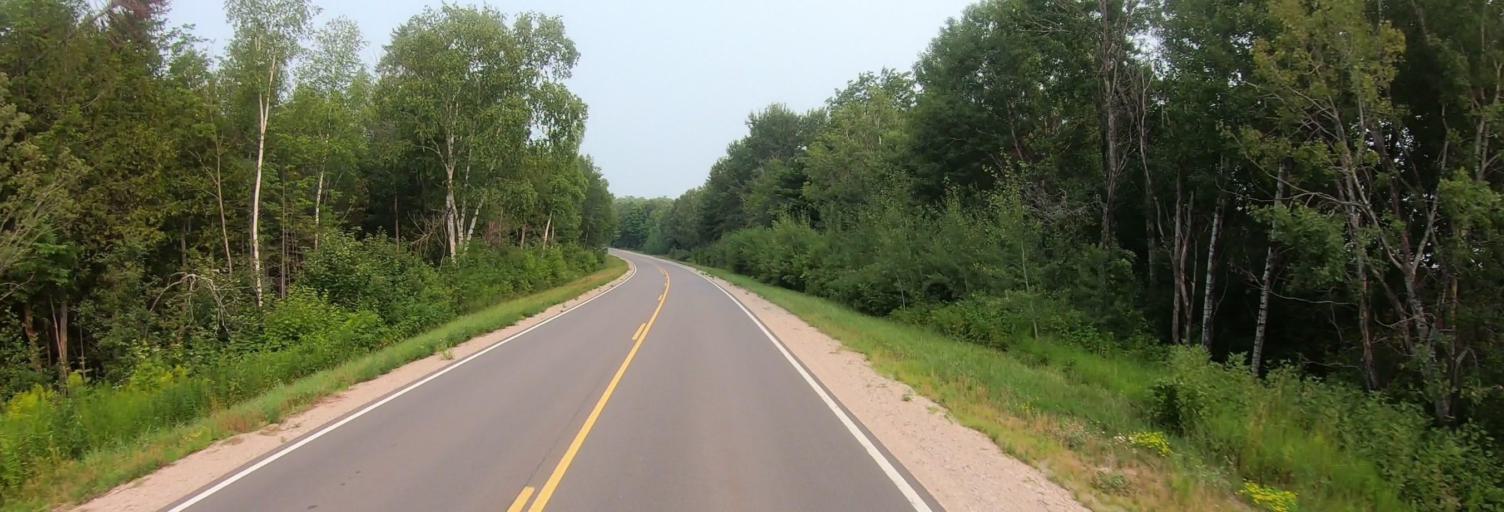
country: US
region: Michigan
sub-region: Luce County
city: Newberry
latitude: 46.4852
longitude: -85.0315
